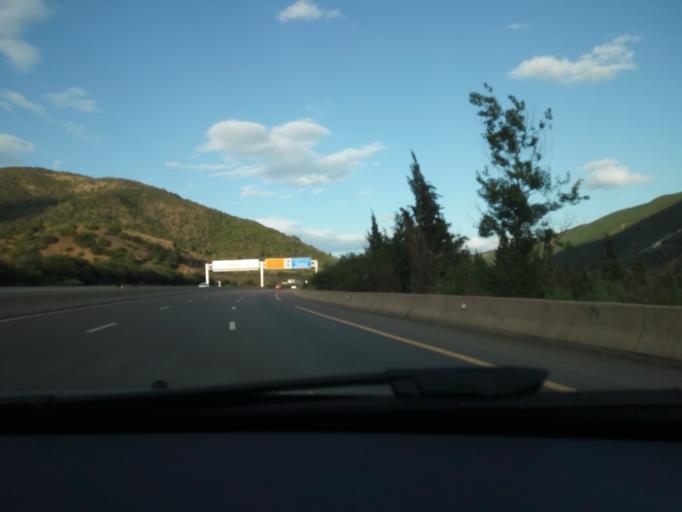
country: DZ
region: Tipaza
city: El Affroun
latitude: 36.3920
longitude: 2.5053
